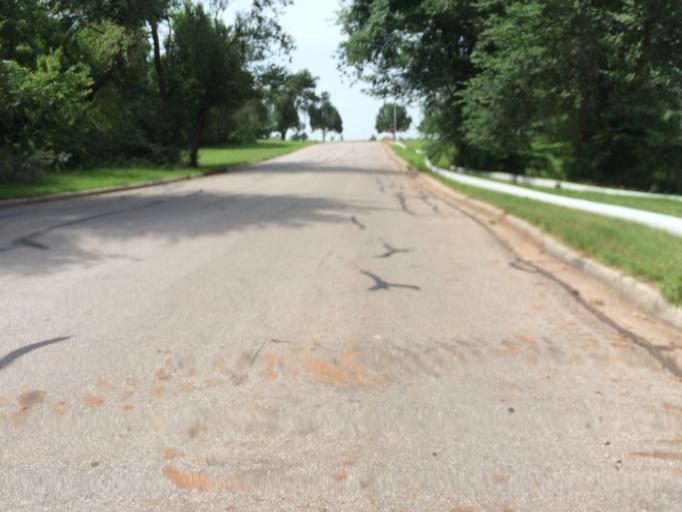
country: US
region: Oklahoma
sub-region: Cleveland County
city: Norman
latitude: 35.1909
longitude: -97.4104
